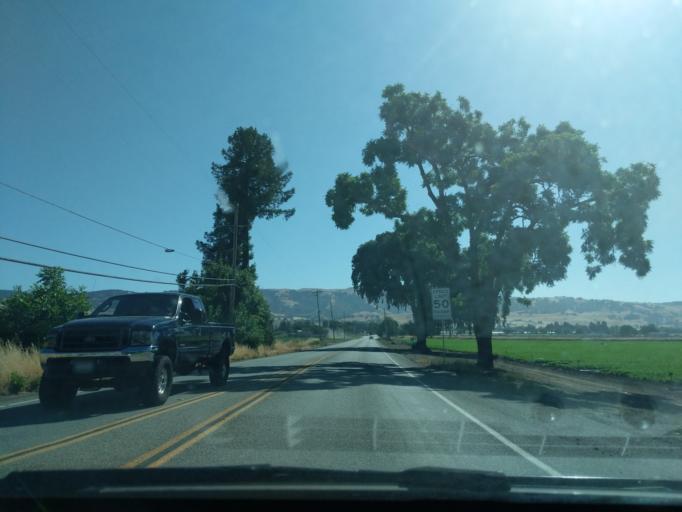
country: US
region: California
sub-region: Santa Clara County
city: Gilroy
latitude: 37.0317
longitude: -121.5422
